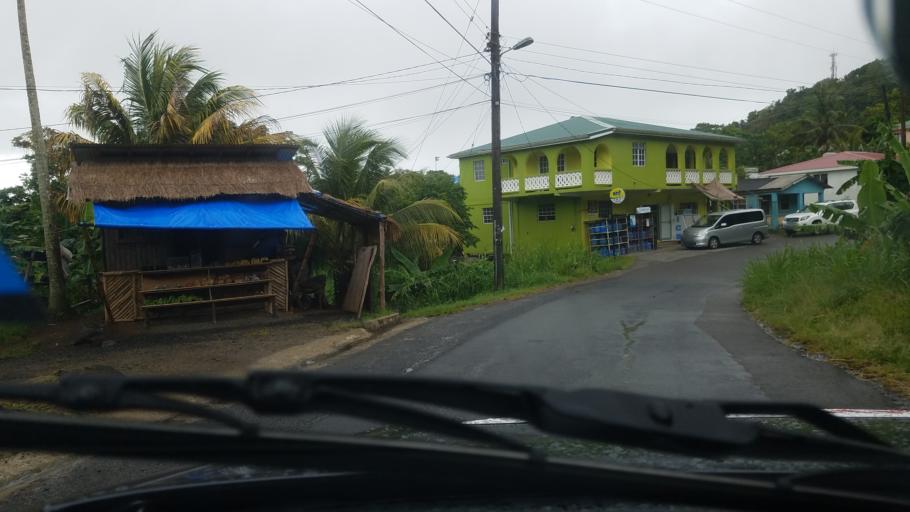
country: LC
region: Castries Quarter
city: Bisee
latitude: 14.0210
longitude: -60.9328
